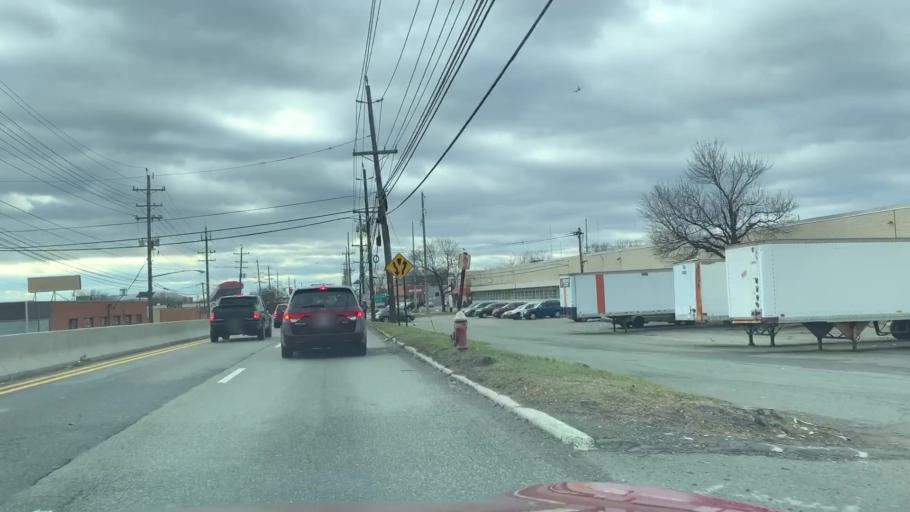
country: US
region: New Jersey
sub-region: Bergen County
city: Moonachie
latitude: 40.8240
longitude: -74.0593
